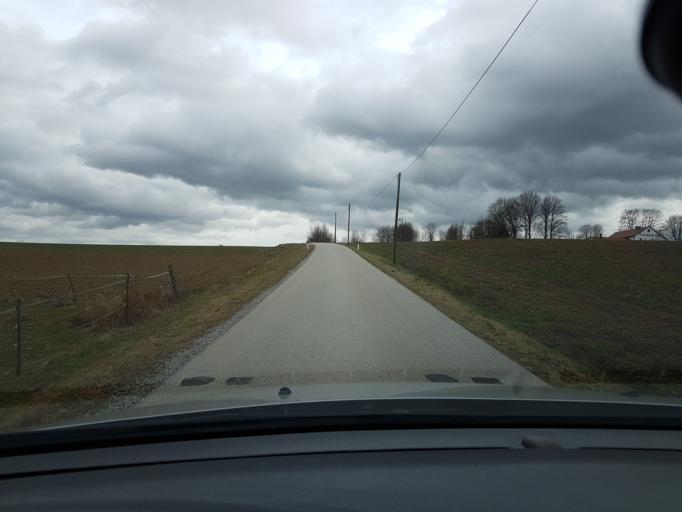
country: DE
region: Bavaria
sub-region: Lower Bavaria
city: Tiefenbach
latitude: 48.5019
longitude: 12.0864
